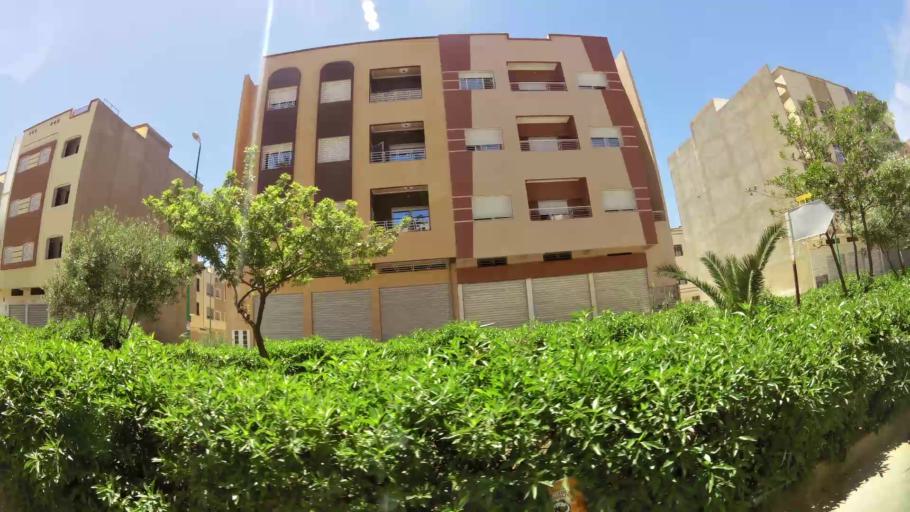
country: MA
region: Meknes-Tafilalet
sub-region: Meknes
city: Meknes
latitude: 33.8563
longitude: -5.5679
